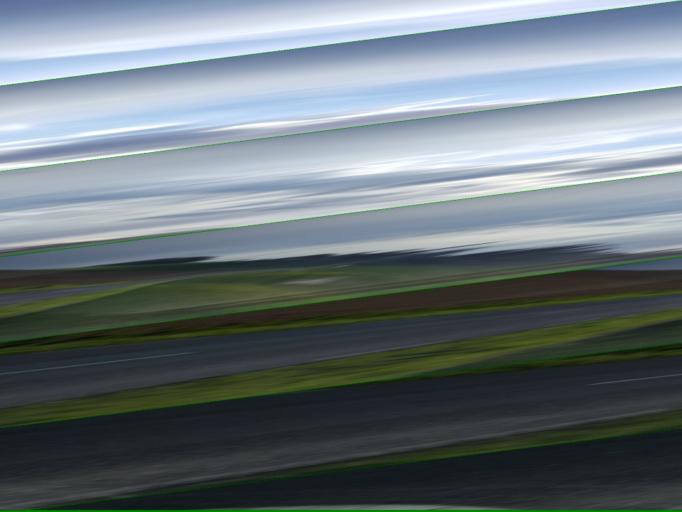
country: FR
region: Ile-de-France
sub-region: Departement du Val-d'Oise
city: Chars
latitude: 49.1900
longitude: 1.8682
